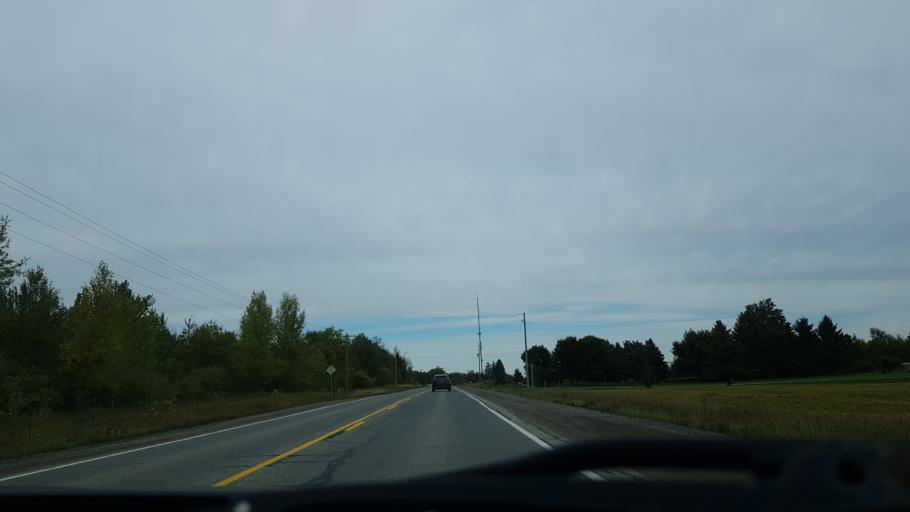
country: CA
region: Ontario
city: Orangeville
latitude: 43.9051
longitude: -79.9465
